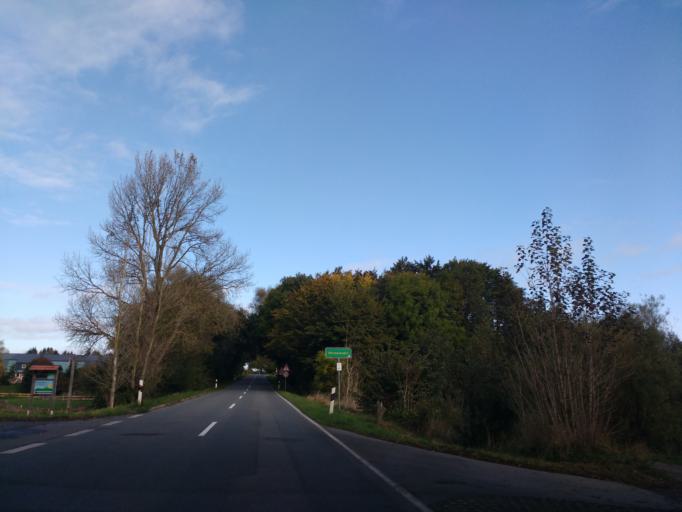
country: DE
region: Schleswig-Holstein
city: Schonwalde am Bungsberg
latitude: 54.2175
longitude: 10.7377
